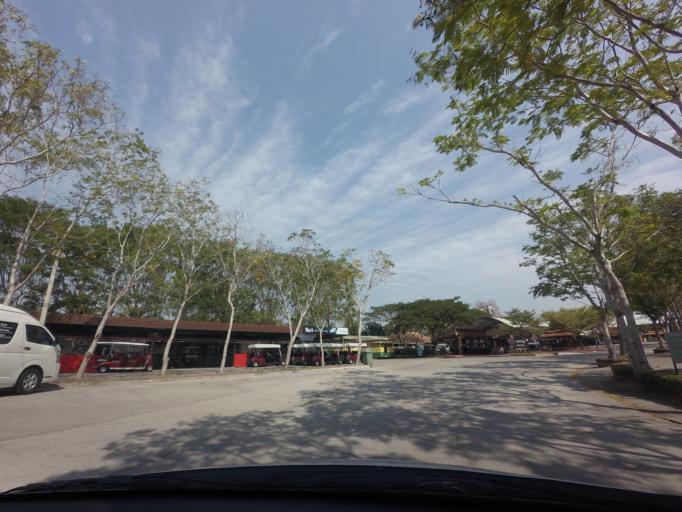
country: TH
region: Samut Prakan
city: Samut Prakan
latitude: 13.5405
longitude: 100.6236
